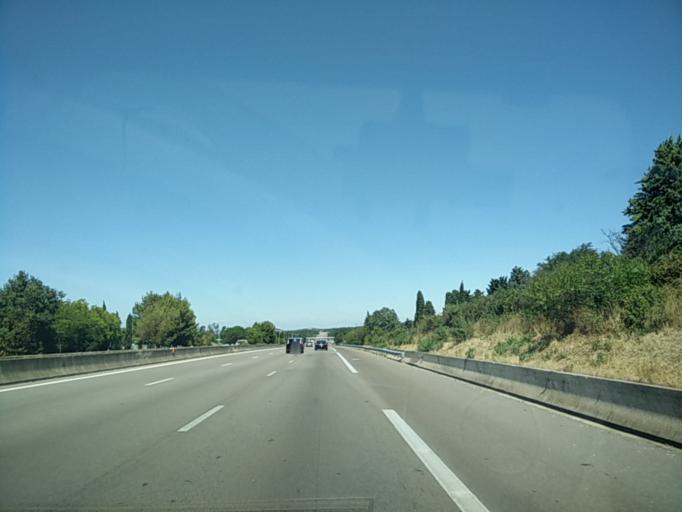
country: FR
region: Provence-Alpes-Cote d'Azur
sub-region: Departement du Vaucluse
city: Morieres-les-Avignon
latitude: 43.9224
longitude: 4.9138
